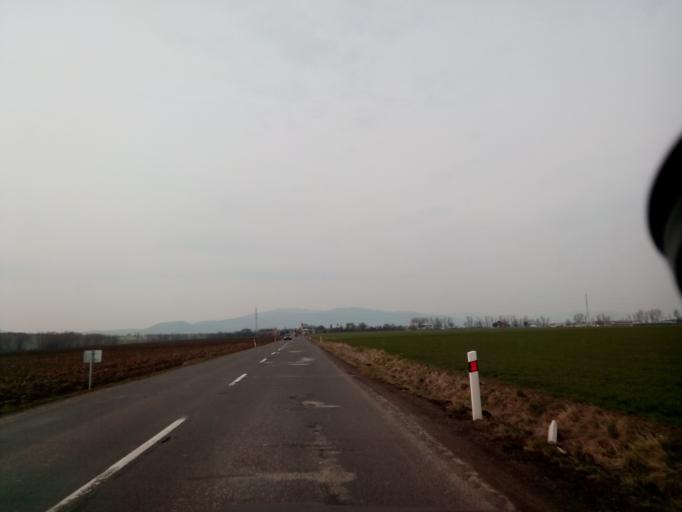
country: SK
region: Kosicky
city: Trebisov
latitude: 48.5911
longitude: 21.6379
